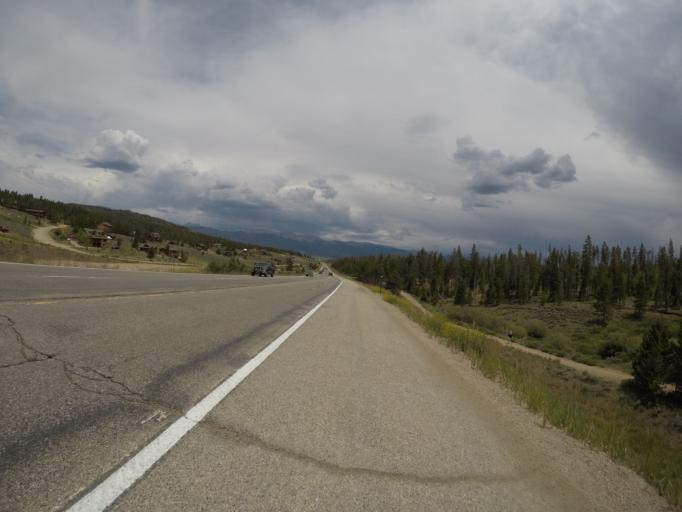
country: US
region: Colorado
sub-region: Grand County
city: Fraser
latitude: 39.9977
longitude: -105.8959
